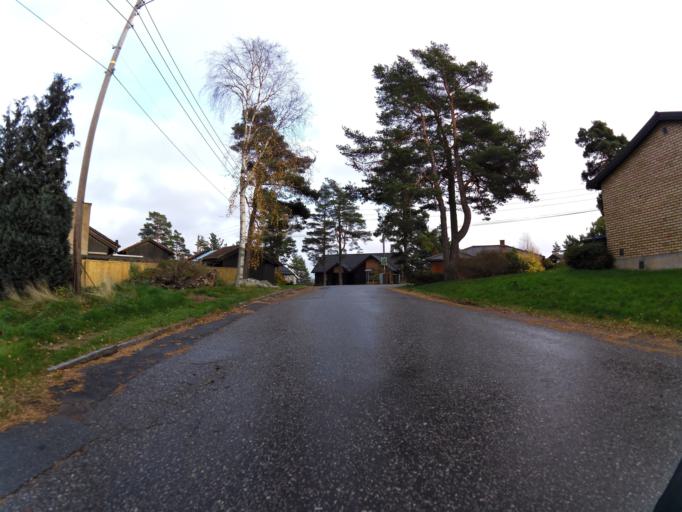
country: NO
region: Ostfold
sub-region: Fredrikstad
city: Fredrikstad
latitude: 59.2278
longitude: 10.9644
